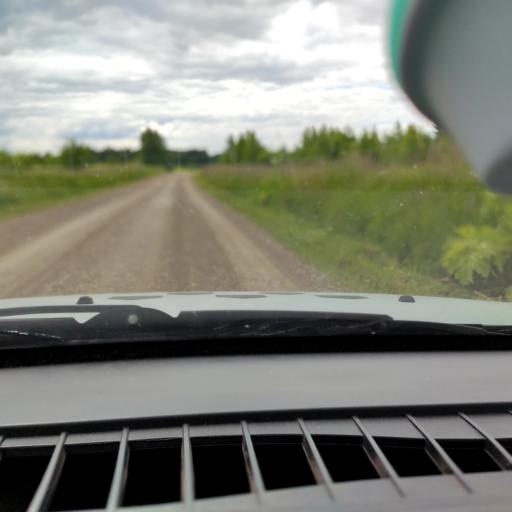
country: RU
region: Perm
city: Suksun
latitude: 57.2021
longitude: 57.6139
